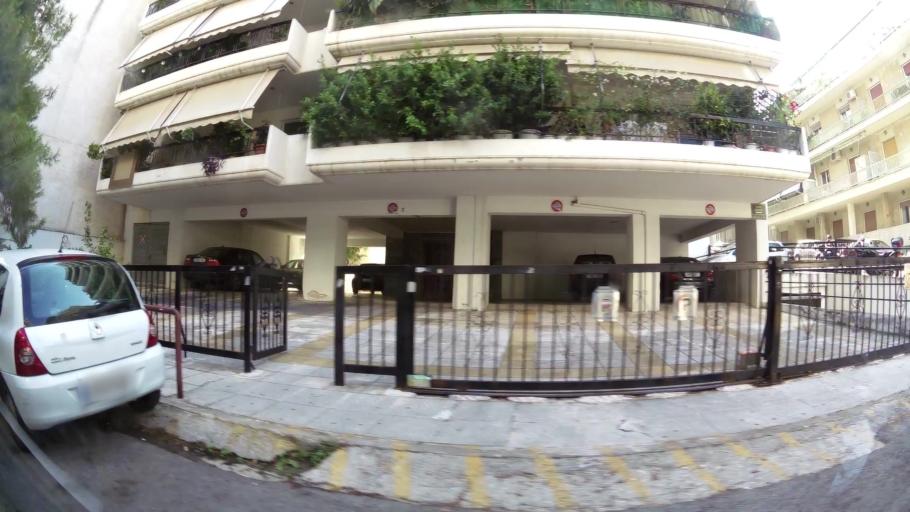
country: GR
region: Attica
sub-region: Nomarchia Athinas
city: Kaisariani
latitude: 37.9800
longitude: 23.7689
